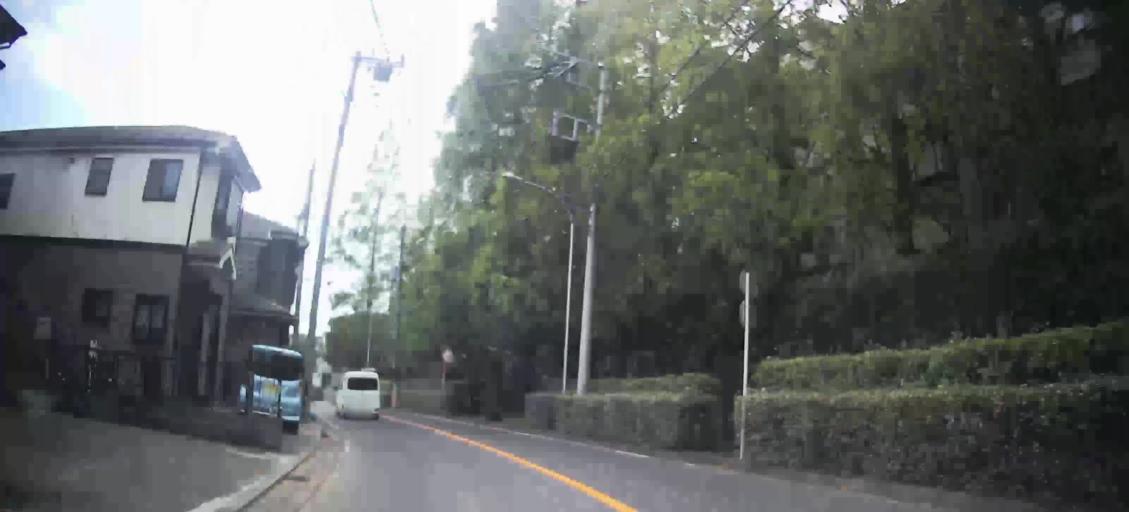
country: JP
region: Kanagawa
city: Yokohama
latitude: 35.4779
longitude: 139.5765
